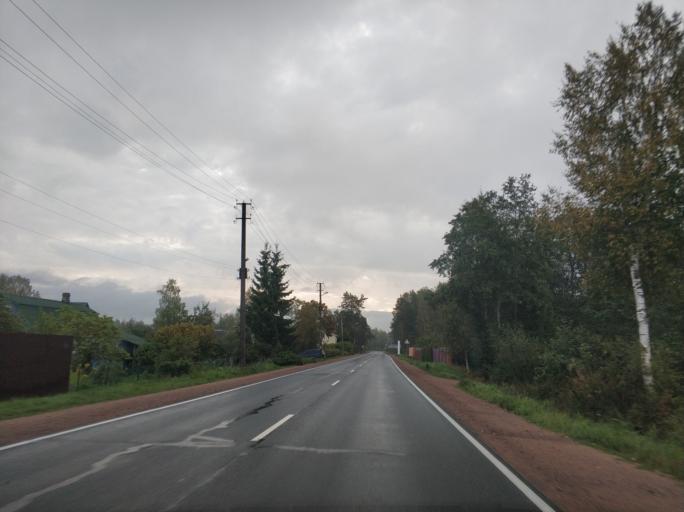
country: RU
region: Leningrad
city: Shcheglovo
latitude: 60.1019
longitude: 30.8021
